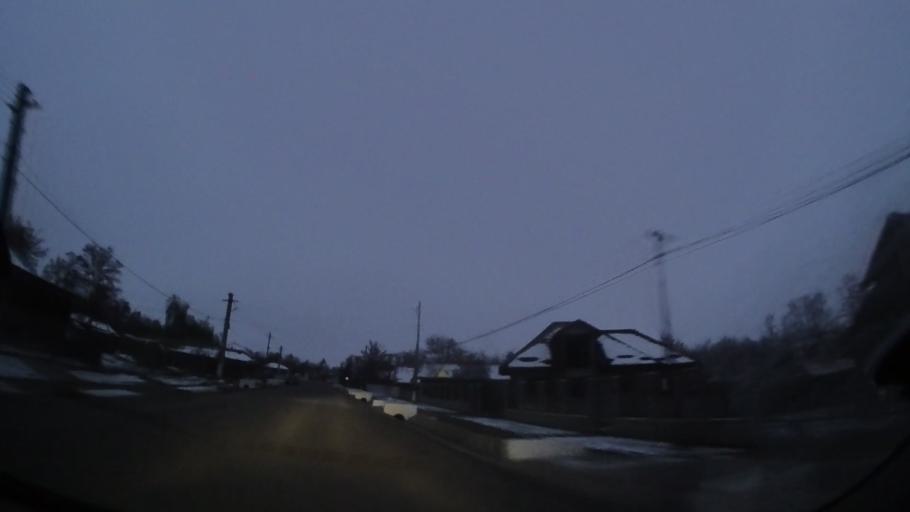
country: RO
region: Vaslui
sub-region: Comuna Dimitrie Cantemir
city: Dimitrie Cantemir
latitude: 46.5052
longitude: 28.0554
